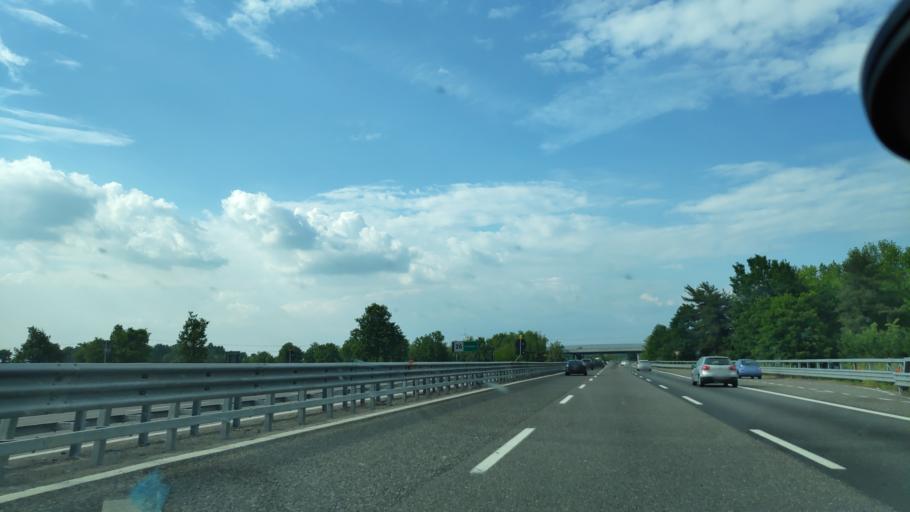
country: IT
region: Lombardy
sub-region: Provincia di Pavia
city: Zerbolo
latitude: 45.2131
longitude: 9.0171
